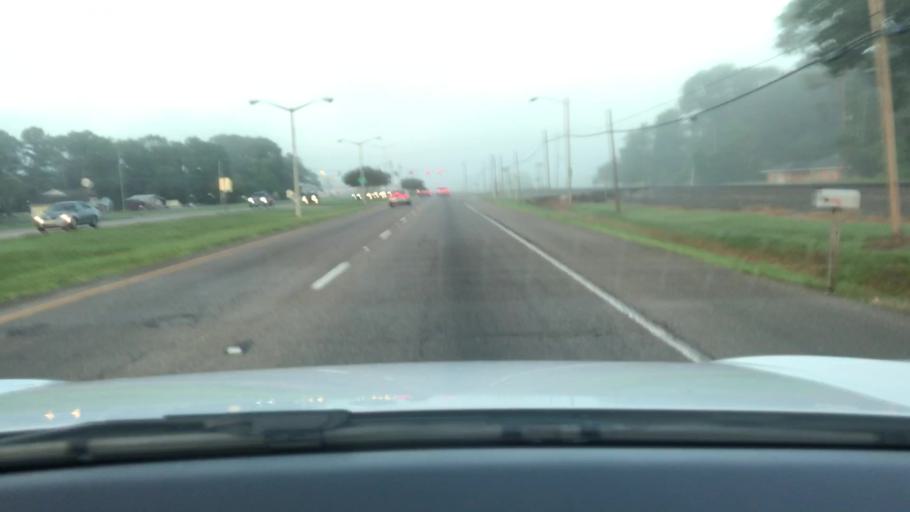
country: US
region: Louisiana
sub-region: West Baton Rouge Parish
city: Brusly
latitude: 30.3917
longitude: -91.2413
